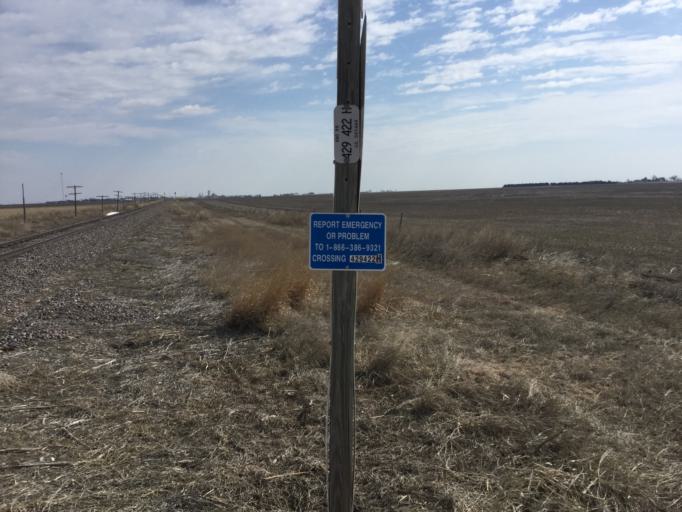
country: US
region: Kansas
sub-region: Lane County
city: Dighton
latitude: 38.5860
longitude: -100.6507
